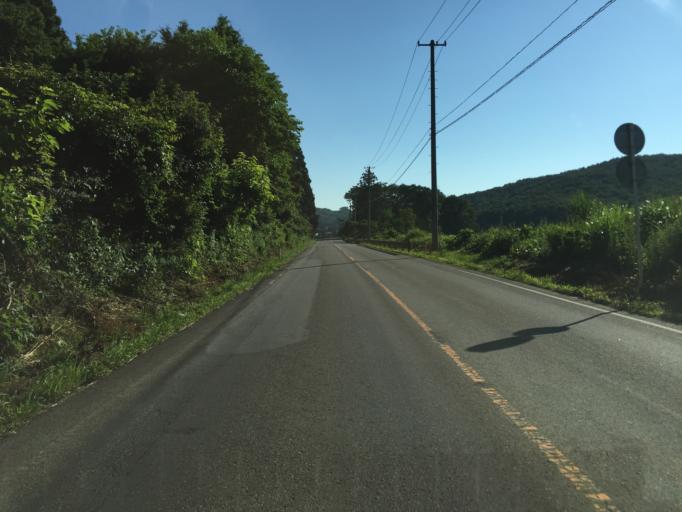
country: JP
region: Miyagi
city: Marumori
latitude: 37.7671
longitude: 140.7422
